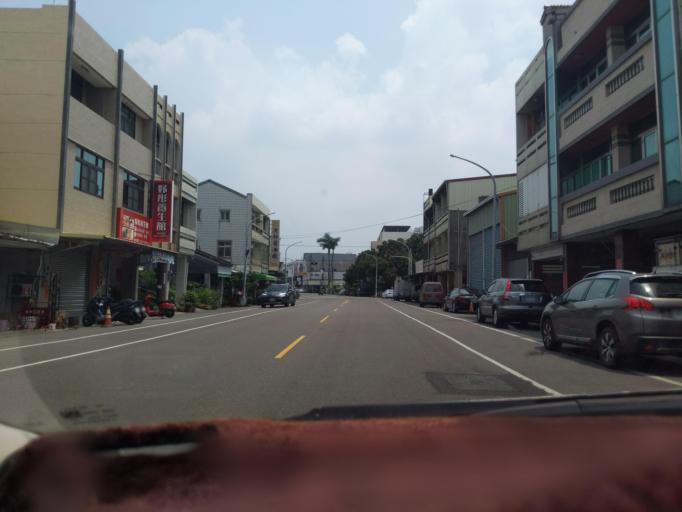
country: TW
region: Taiwan
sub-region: Yunlin
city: Douliu
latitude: 23.8018
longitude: 120.4648
